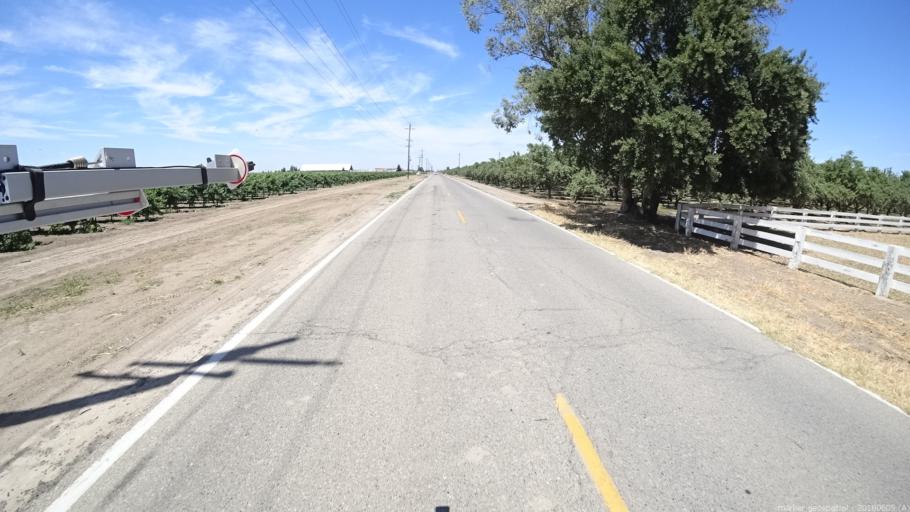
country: US
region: California
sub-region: Merced County
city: Dos Palos
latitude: 37.0739
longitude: -120.4735
